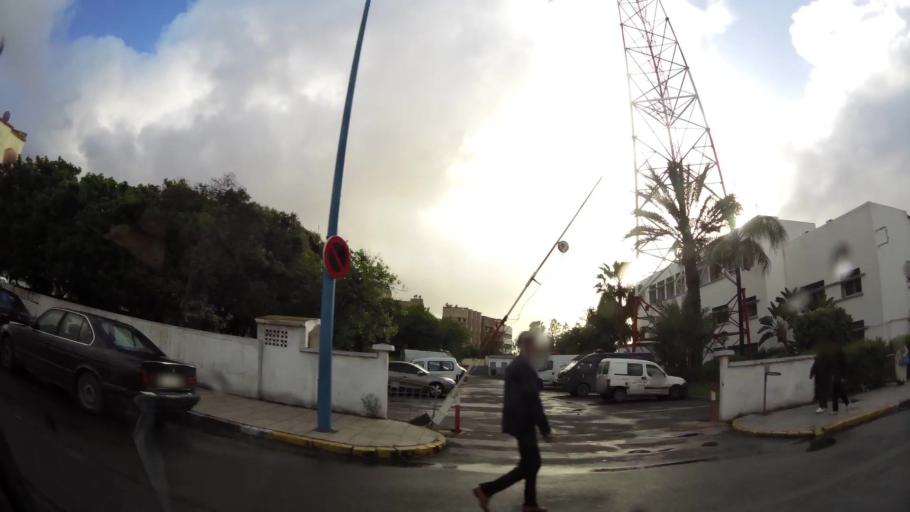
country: MA
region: Grand Casablanca
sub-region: Casablanca
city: Casablanca
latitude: 33.5574
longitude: -7.5732
